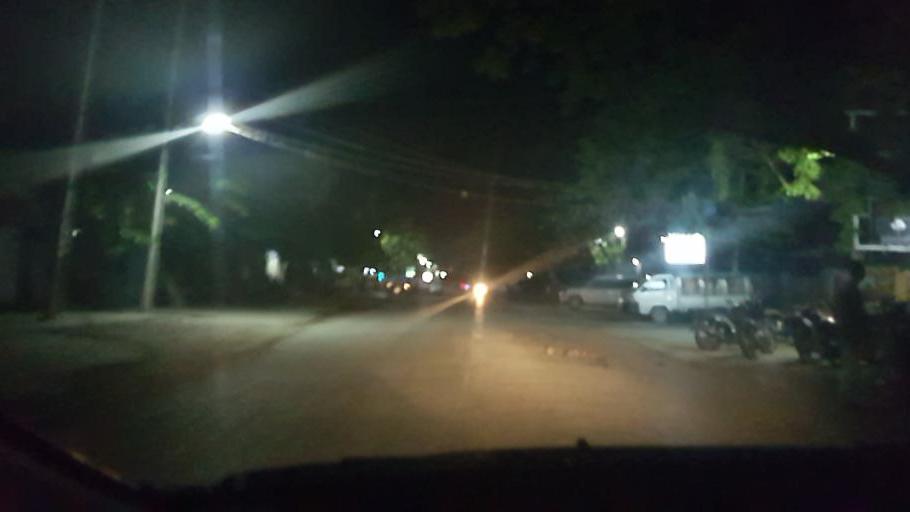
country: MM
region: Mandalay
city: Mandalay
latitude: 21.9799
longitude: 96.0937
